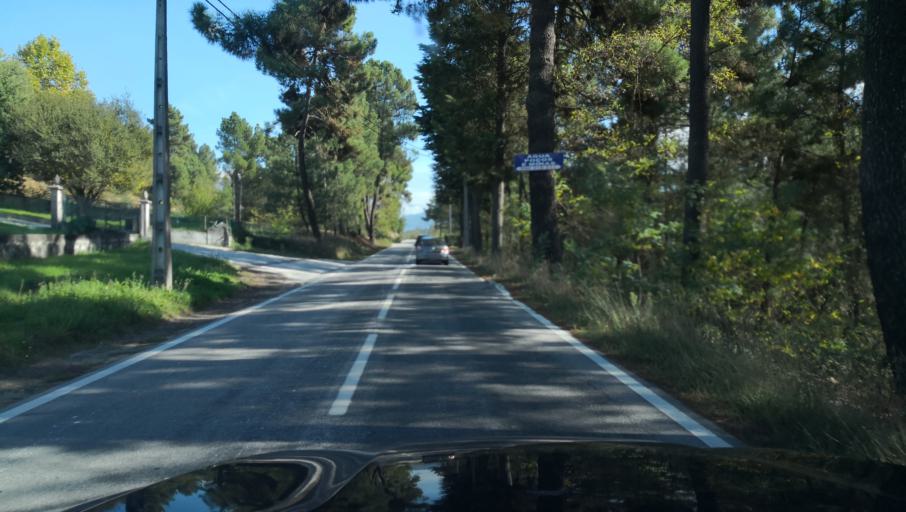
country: PT
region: Vila Real
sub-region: Chaves
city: Chaves
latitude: 41.7206
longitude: -7.4957
